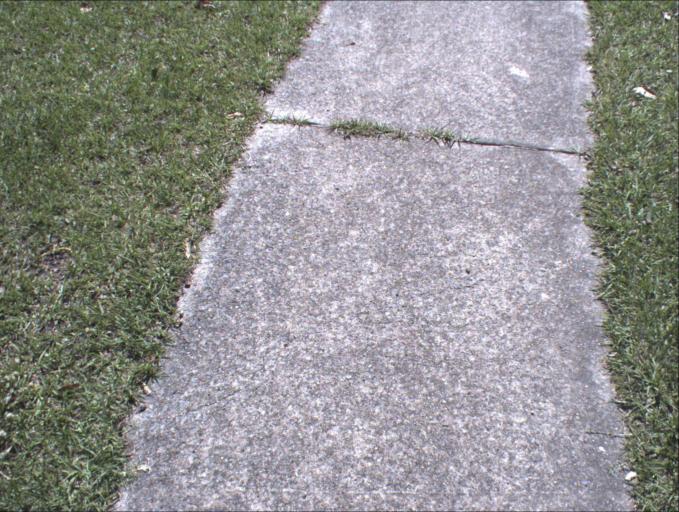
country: AU
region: Queensland
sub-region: Logan
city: Waterford West
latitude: -27.7053
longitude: 153.1615
